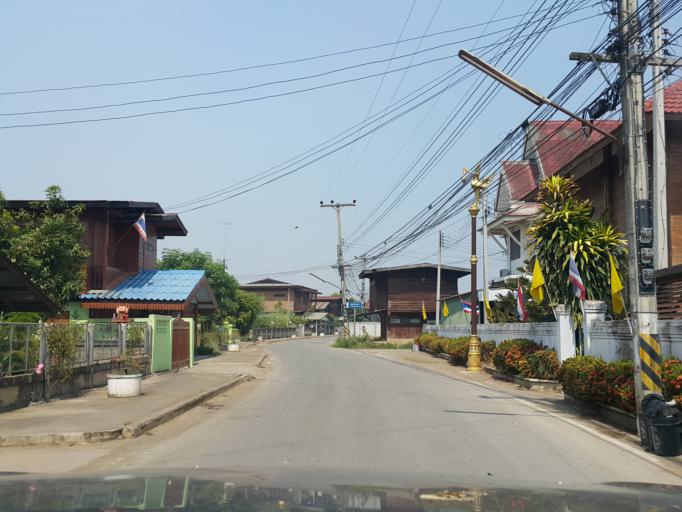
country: TH
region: Sukhothai
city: Thung Saliam
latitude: 17.3121
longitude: 99.5525
